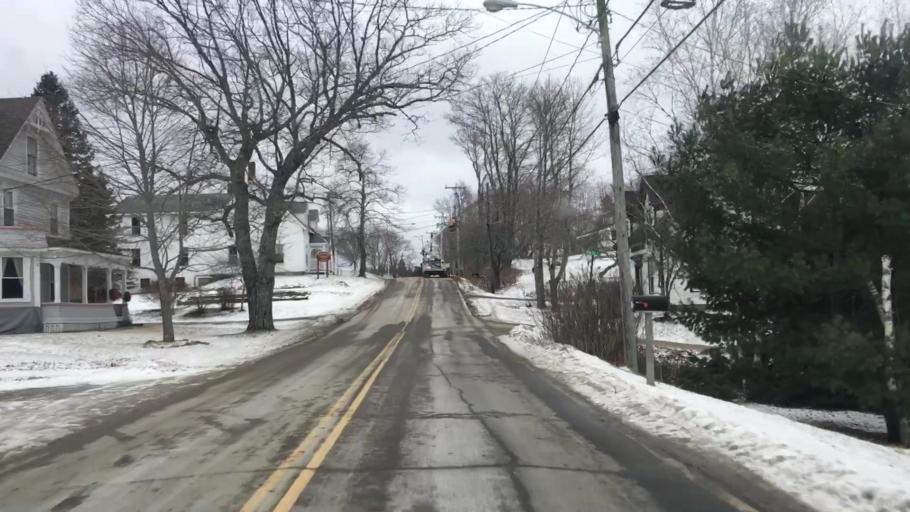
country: US
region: Maine
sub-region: Washington County
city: East Machias
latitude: 44.7357
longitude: -67.3887
